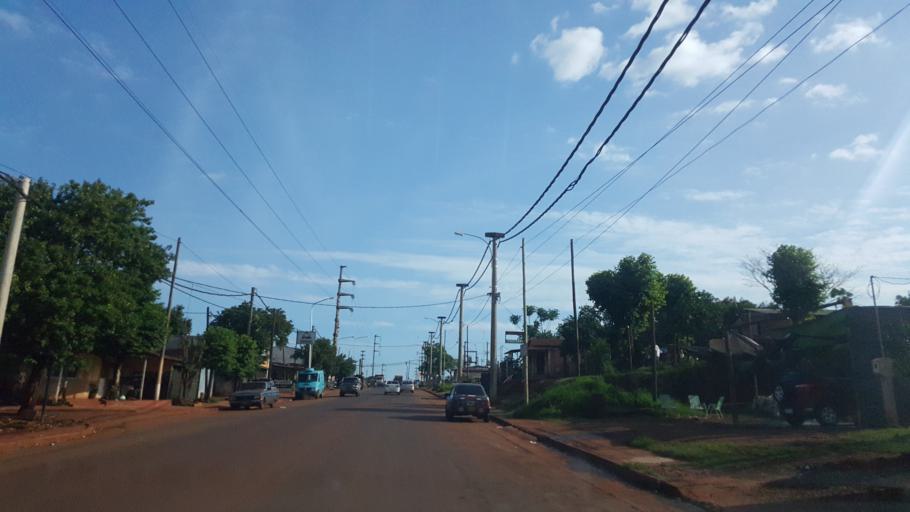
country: AR
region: Misiones
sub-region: Departamento de Capital
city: Posadas
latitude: -27.4260
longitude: -55.9140
